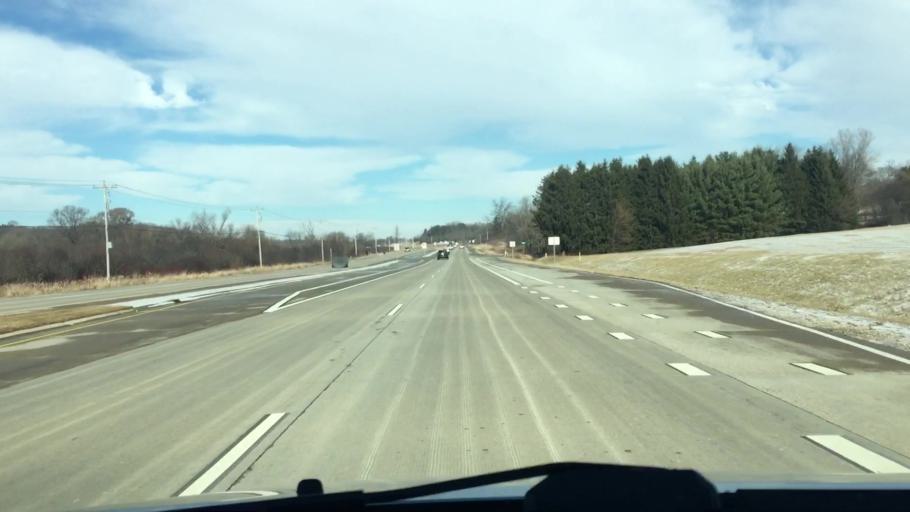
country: US
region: Wisconsin
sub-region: Waukesha County
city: Mukwonago
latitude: 42.8908
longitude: -88.3436
